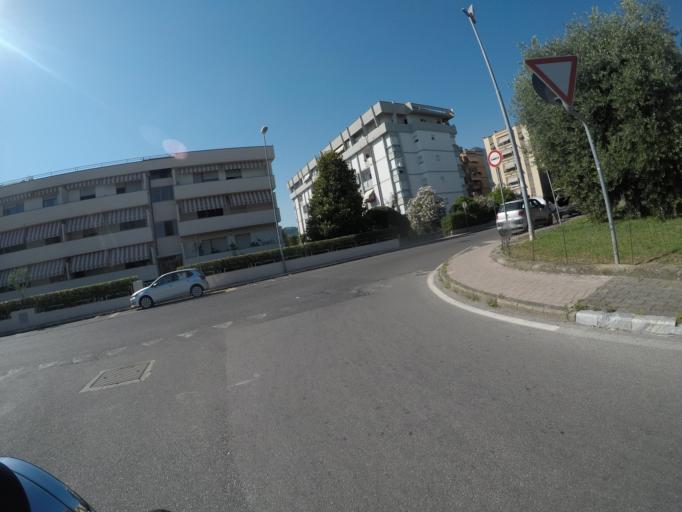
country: IT
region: Tuscany
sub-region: Provincia di Massa-Carrara
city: Massa
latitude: 44.0331
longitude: 10.1329
